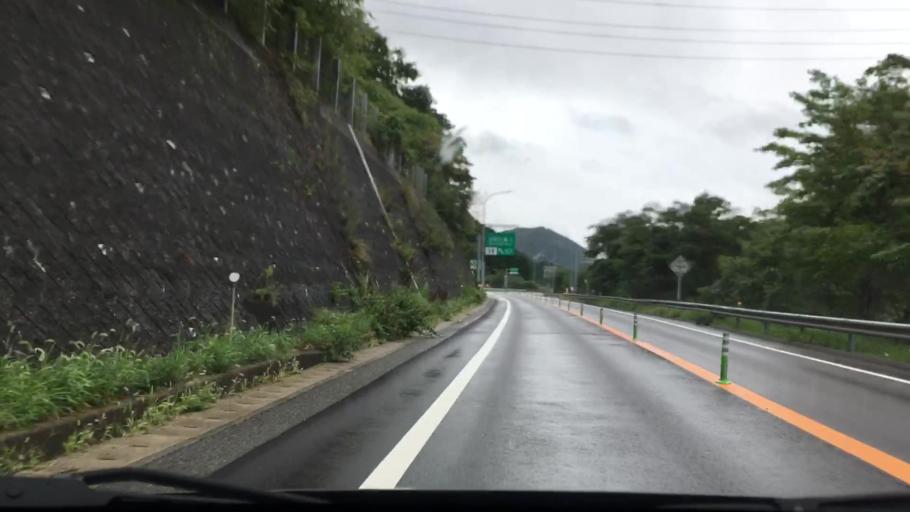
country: JP
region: Hyogo
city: Nishiwaki
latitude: 35.1838
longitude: 134.7923
